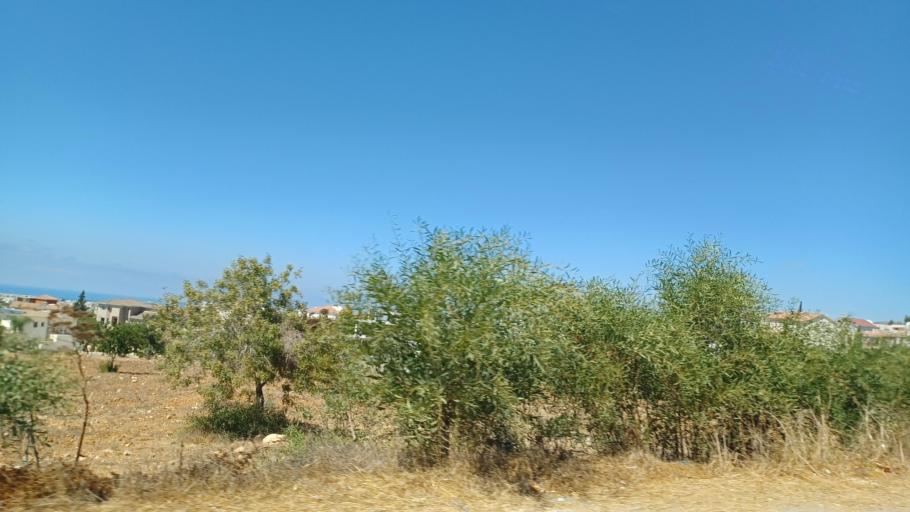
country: CY
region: Pafos
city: Paphos
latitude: 34.7786
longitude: 32.4615
